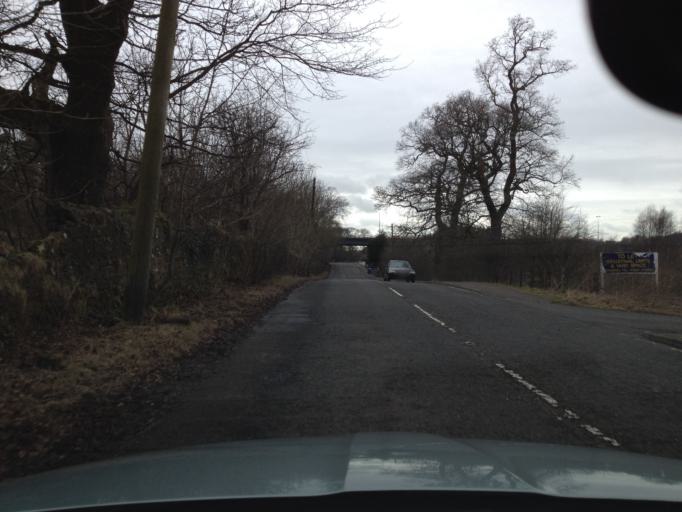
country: GB
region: Scotland
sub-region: West Lothian
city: Mid Calder
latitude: 55.8887
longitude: -3.4977
